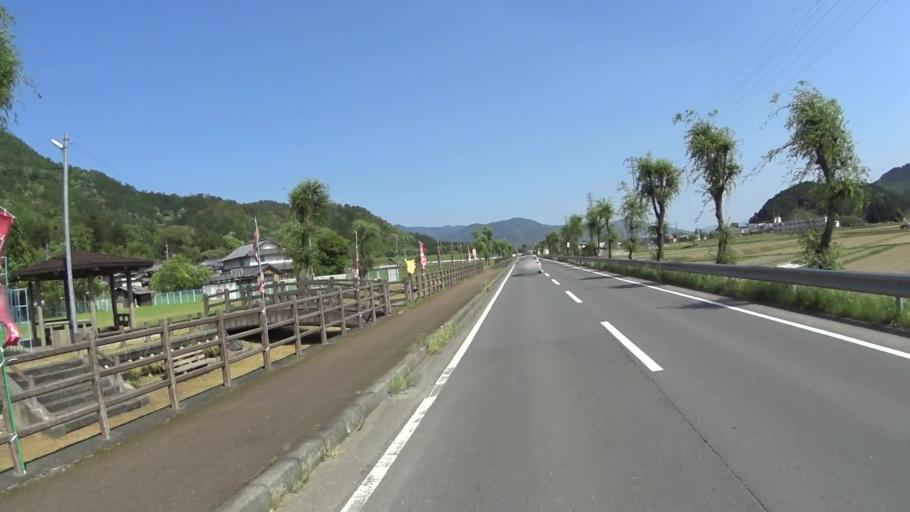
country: JP
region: Kyoto
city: Kameoka
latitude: 35.1090
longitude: 135.5207
